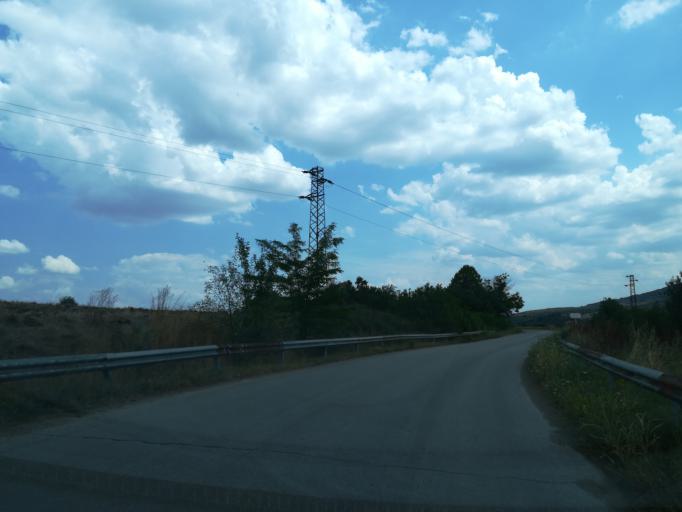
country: BG
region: Khaskovo
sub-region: Obshtina Mineralni Bani
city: Mineralni Bani
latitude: 41.9828
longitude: 25.1661
